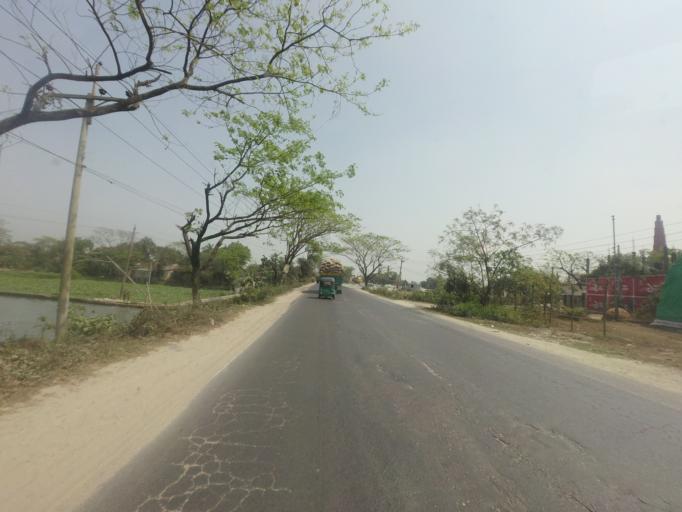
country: BD
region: Dhaka
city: Bhairab Bazar
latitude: 24.0403
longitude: 91.0369
